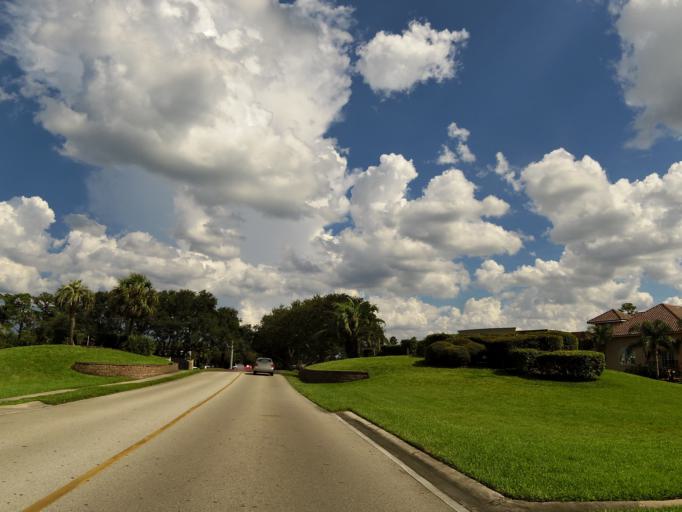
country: US
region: Florida
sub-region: Saint Johns County
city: Ponte Vedra Beach
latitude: 30.2488
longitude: -81.3891
